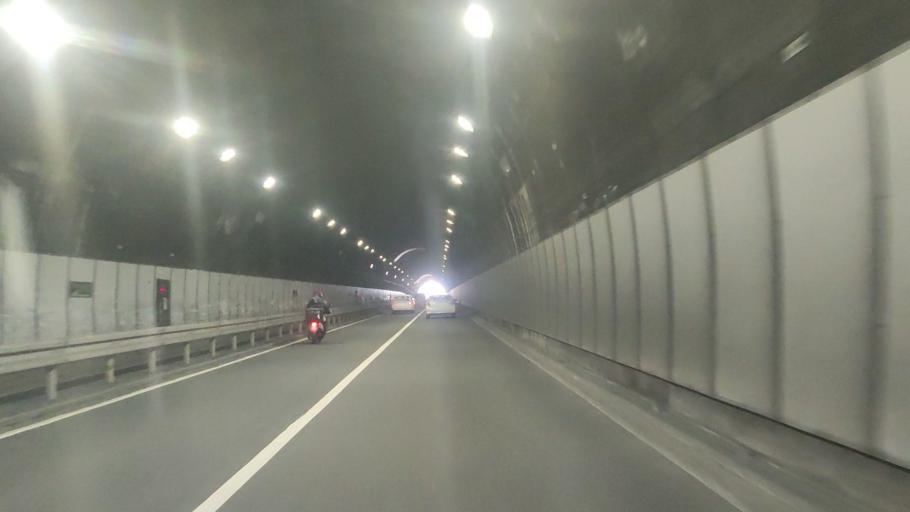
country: JP
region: Oita
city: Oita
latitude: 33.2201
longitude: 131.5948
